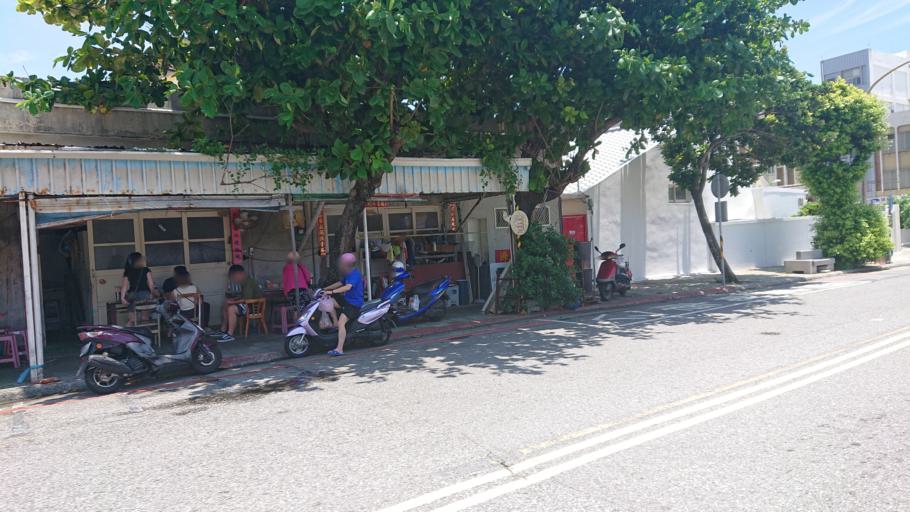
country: TW
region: Taiwan
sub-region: Penghu
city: Ma-kung
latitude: 23.5672
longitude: 119.5642
